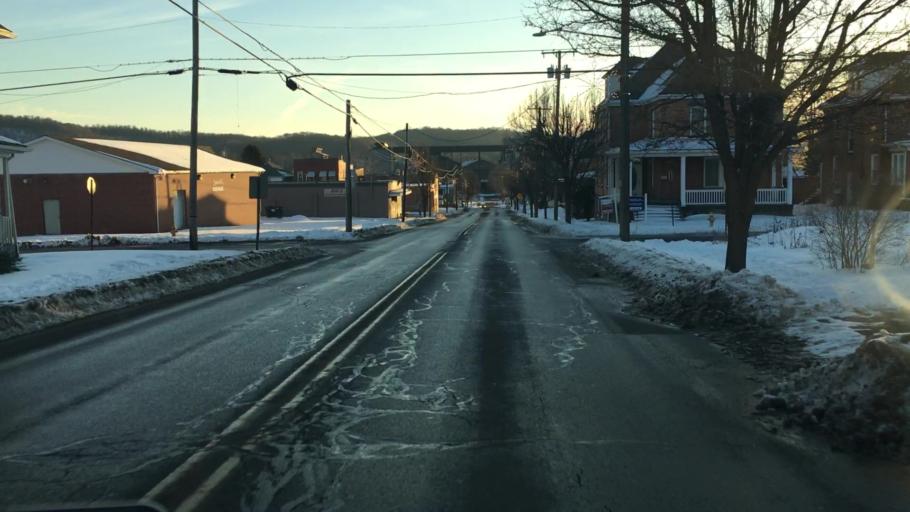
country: US
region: Pennsylvania
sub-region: Beaver County
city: Big Beaver
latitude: 40.8343
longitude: -80.3266
